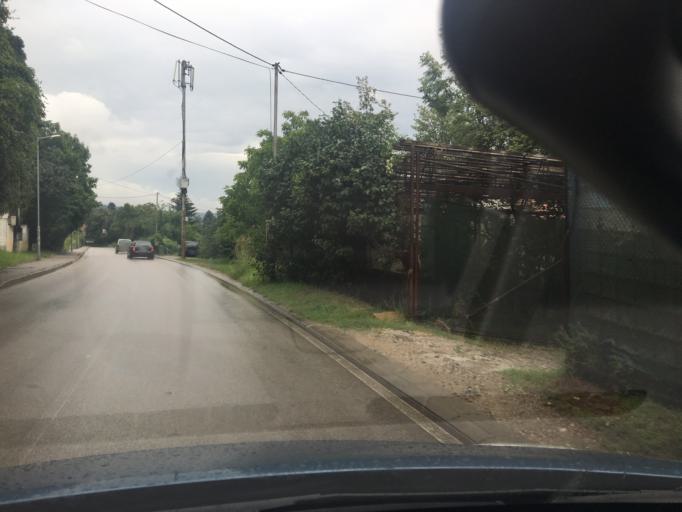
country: BG
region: Sofia-Capital
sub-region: Stolichna Obshtina
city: Sofia
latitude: 42.6454
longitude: 23.2768
